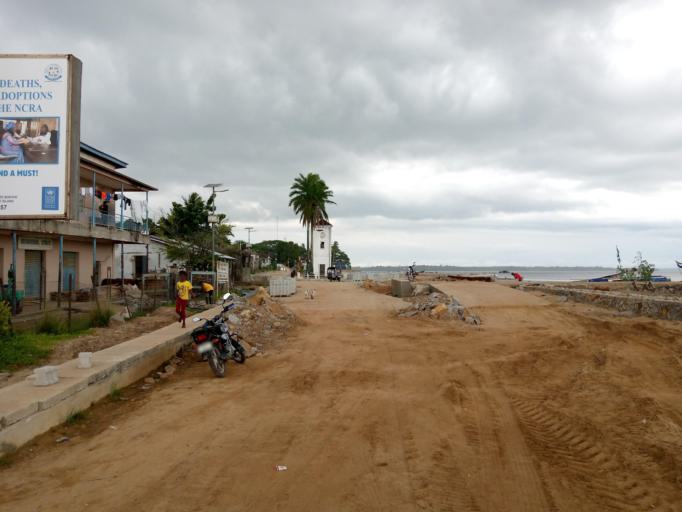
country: SL
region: Southern Province
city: Bonthe
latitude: 7.5300
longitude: -12.5011
